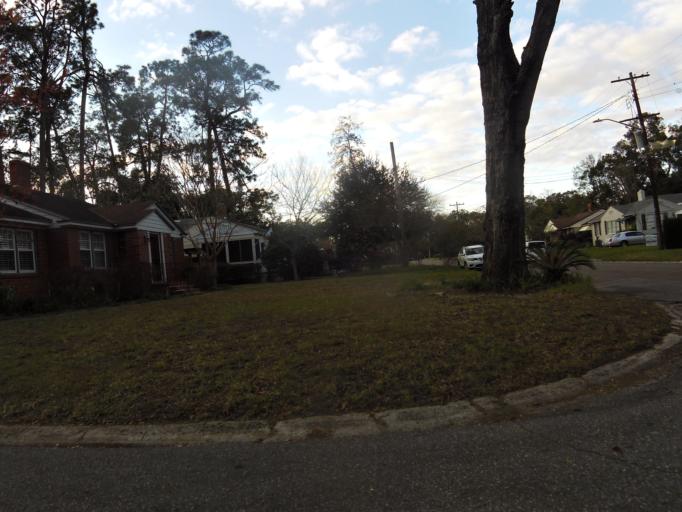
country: US
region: Florida
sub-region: Duval County
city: Jacksonville
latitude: 30.2938
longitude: -81.7178
